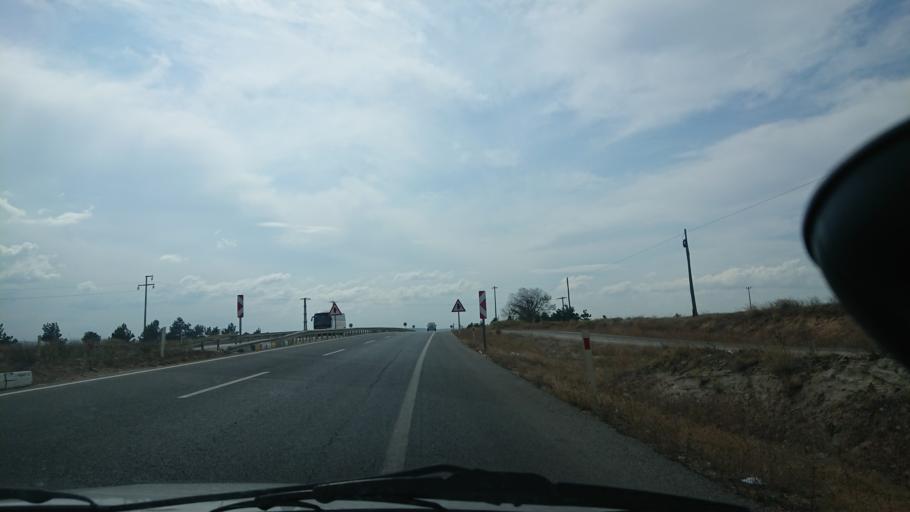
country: TR
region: Eskisehir
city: Inonu
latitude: 39.7148
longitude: 30.1845
